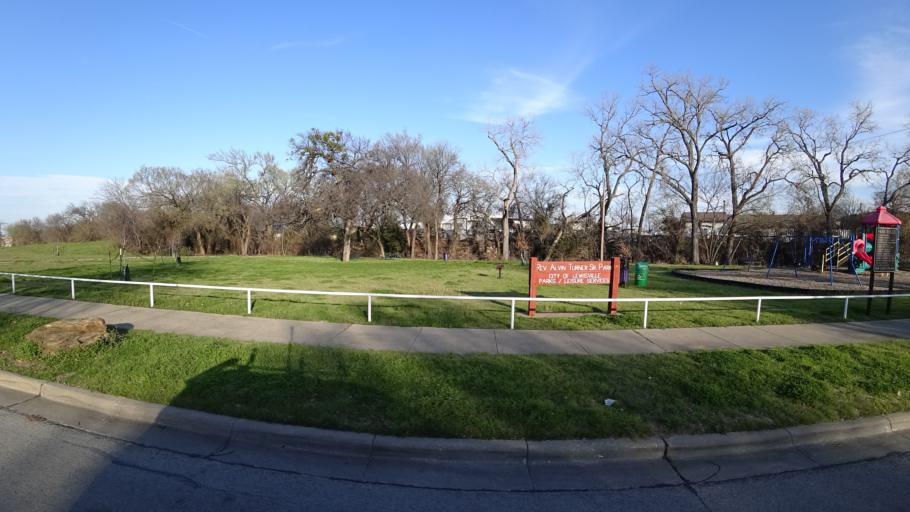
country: US
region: Texas
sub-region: Denton County
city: Lewisville
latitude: 33.0382
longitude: -96.9897
